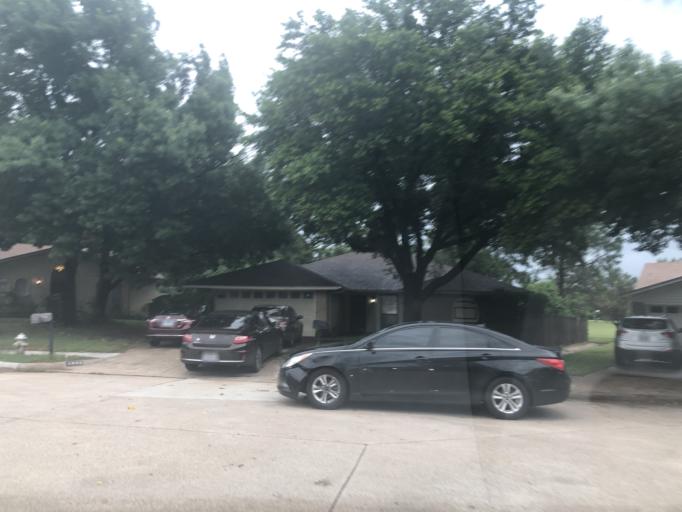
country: US
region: Texas
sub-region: Dallas County
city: Irving
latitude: 32.7958
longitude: -96.9416
